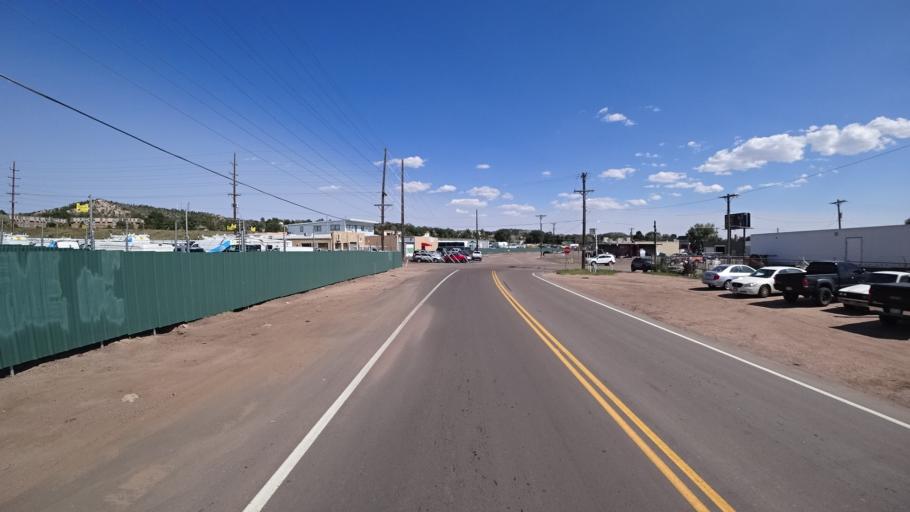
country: US
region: Colorado
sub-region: El Paso County
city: Colorado Springs
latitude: 38.8860
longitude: -104.8132
